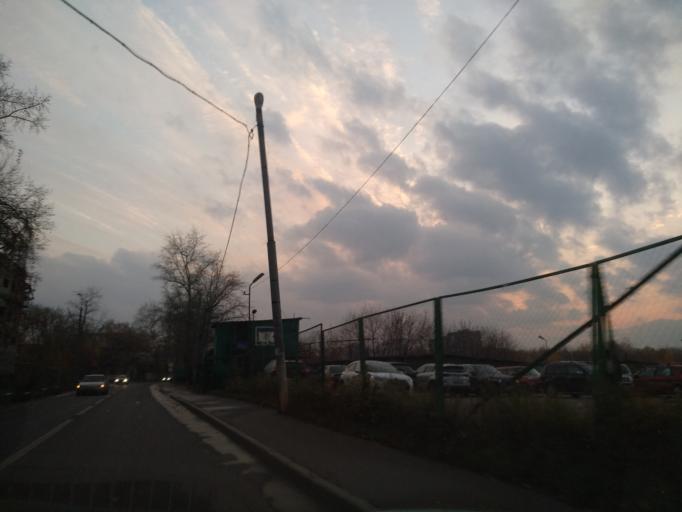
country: RU
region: Moscow
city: Leonovo
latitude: 55.8651
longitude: 37.6501
